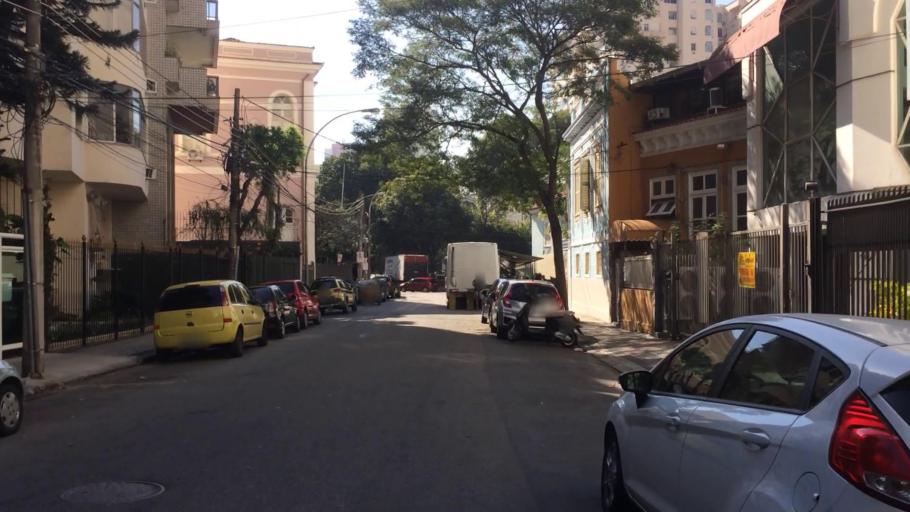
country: BR
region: Rio de Janeiro
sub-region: Rio De Janeiro
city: Rio de Janeiro
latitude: -22.9342
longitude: -43.1816
